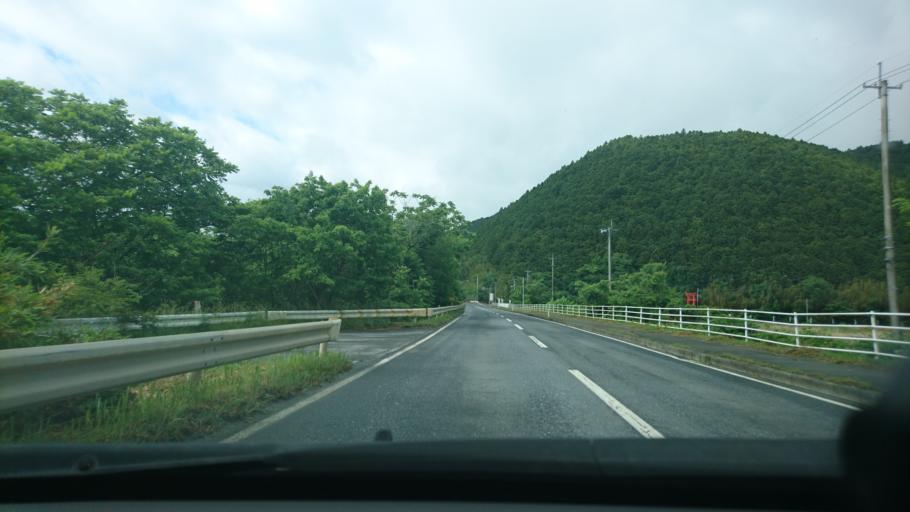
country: JP
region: Miyagi
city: Ishinomaki
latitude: 38.5883
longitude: 141.3044
